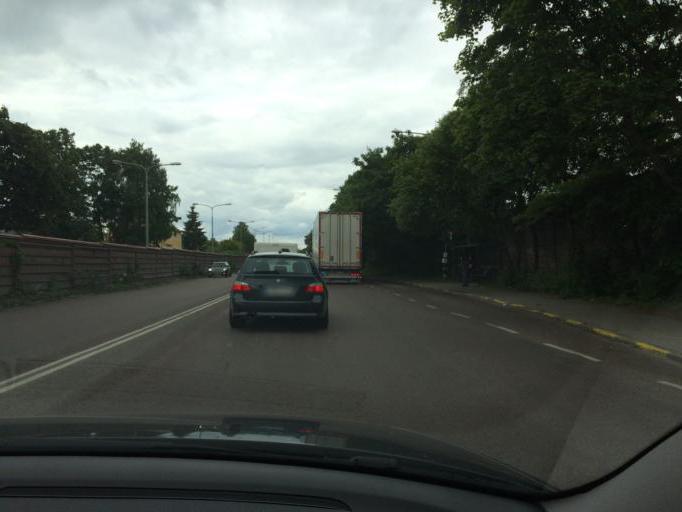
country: SE
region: Stockholm
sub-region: Stockholms Kommun
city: Kista
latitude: 59.3754
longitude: 17.9138
